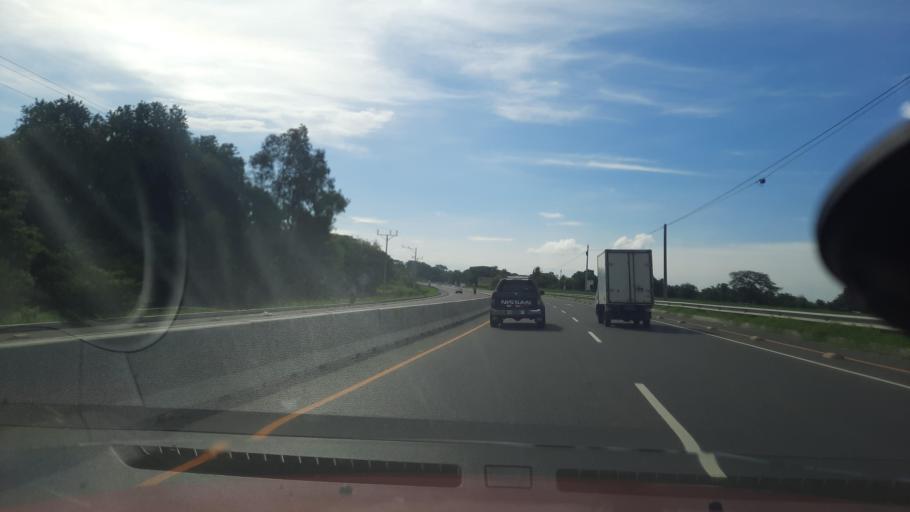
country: SV
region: La Paz
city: El Rosario
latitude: 13.4749
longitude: -89.0486
